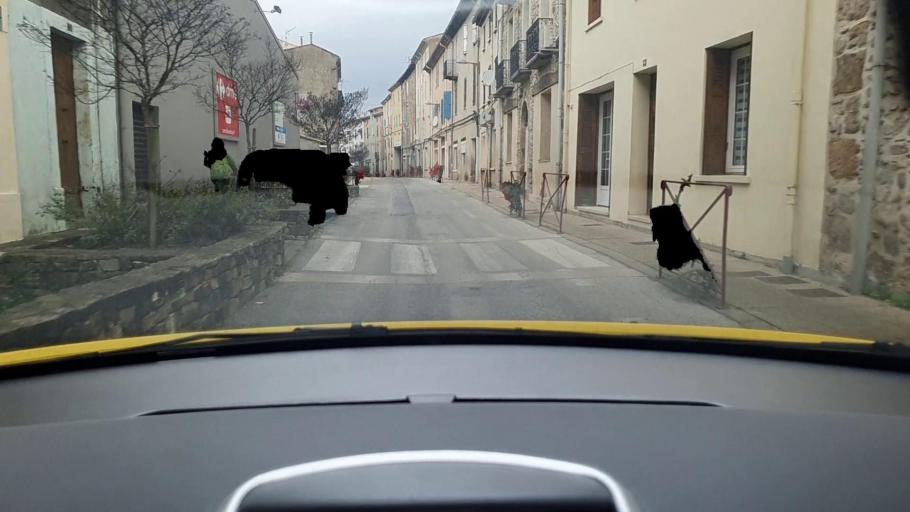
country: FR
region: Languedoc-Roussillon
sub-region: Departement du Gard
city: Besseges
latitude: 44.2894
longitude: 4.1043
